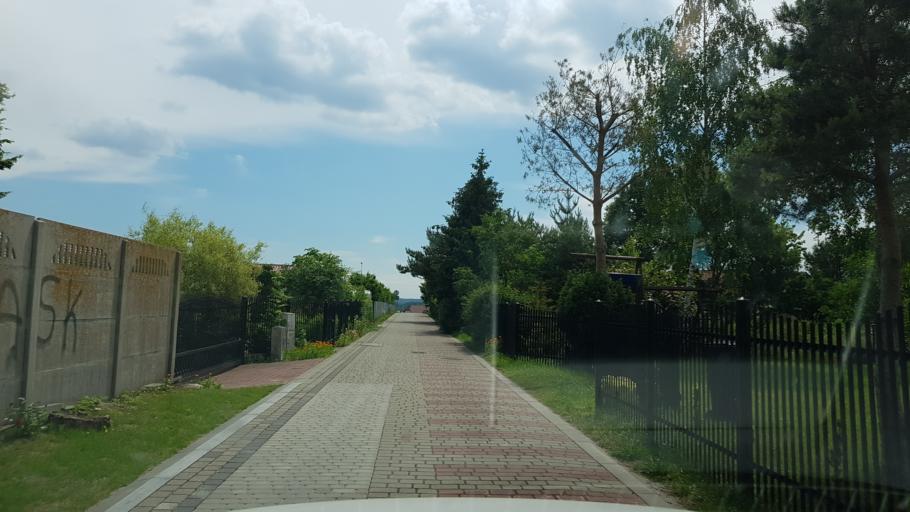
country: PL
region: West Pomeranian Voivodeship
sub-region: Powiat slawienski
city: Darlowo
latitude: 54.5402
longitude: 16.5345
